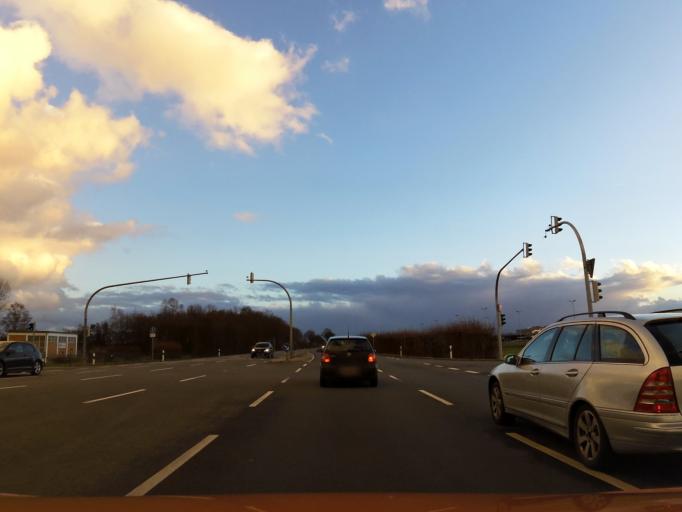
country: DE
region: Lower Saxony
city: Klein Schwulper
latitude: 52.3479
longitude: 10.4087
